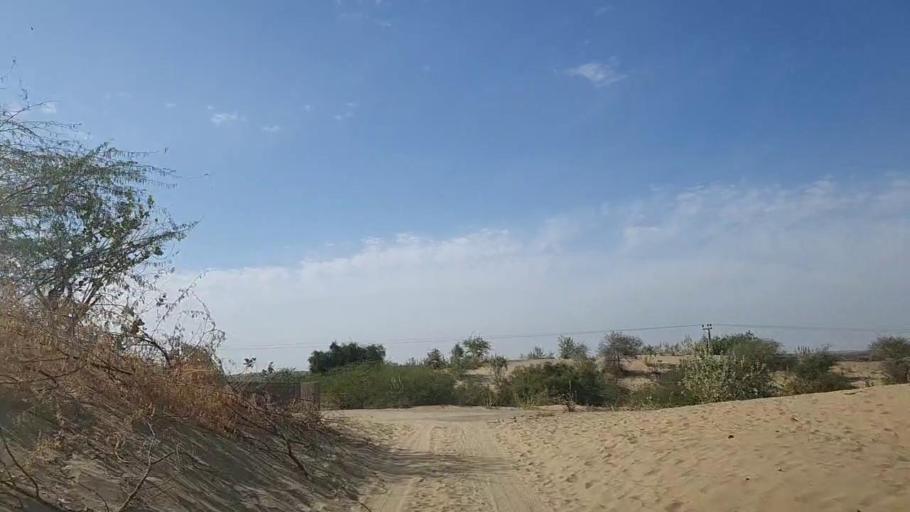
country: PK
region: Sindh
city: Naukot
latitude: 24.8220
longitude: 69.5399
